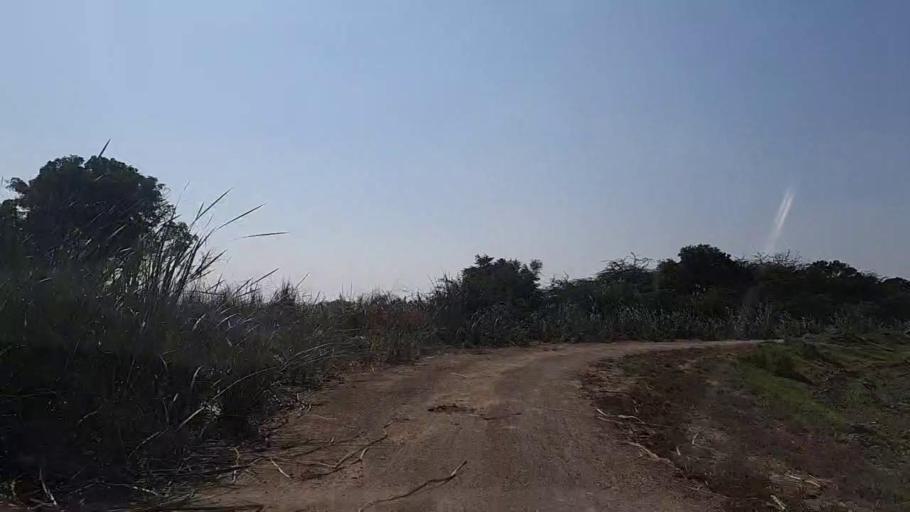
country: PK
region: Sindh
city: Thatta
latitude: 24.7855
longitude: 67.9344
